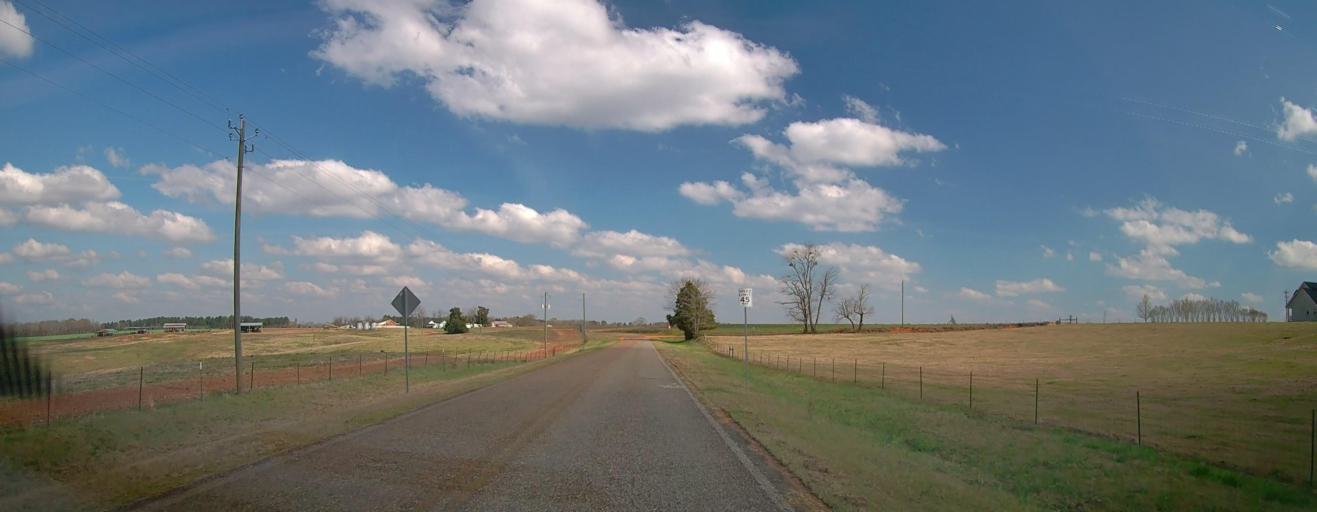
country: US
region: Georgia
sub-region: Twiggs County
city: Jeffersonville
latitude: 32.6546
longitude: -83.2166
